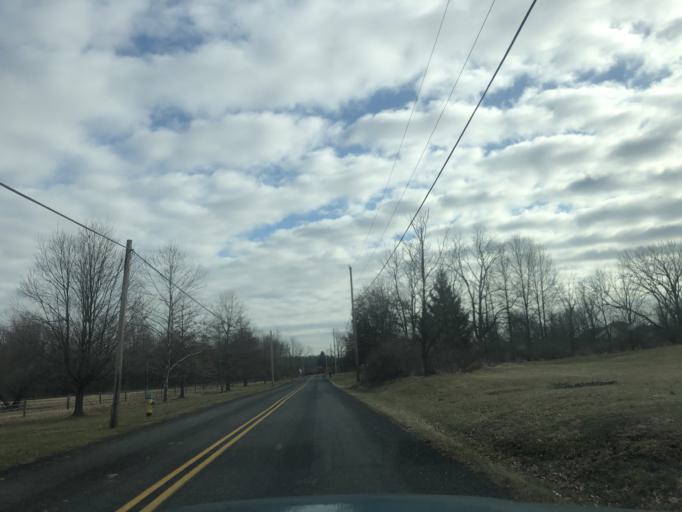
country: US
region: Pennsylvania
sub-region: Bucks County
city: Spinnerstown
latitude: 40.4452
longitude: -75.4190
